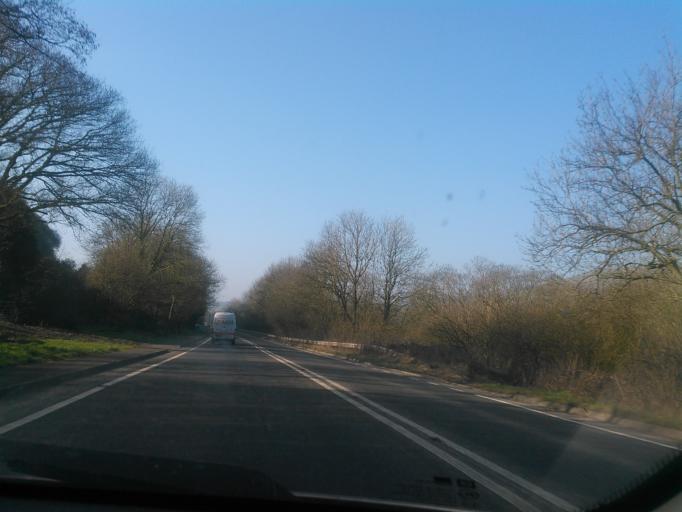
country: GB
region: England
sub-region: Shropshire
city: Church Stretton
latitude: 52.5276
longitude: -2.8129
